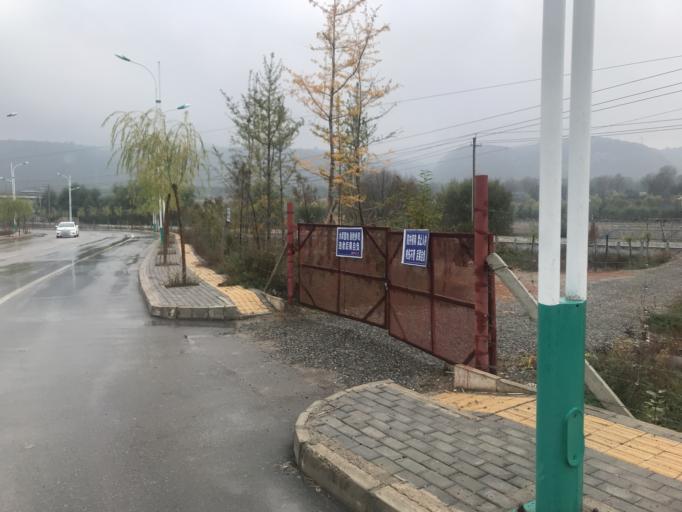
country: CN
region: Gansu Sheng
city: Hanji
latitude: 35.4885
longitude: 103.0620
